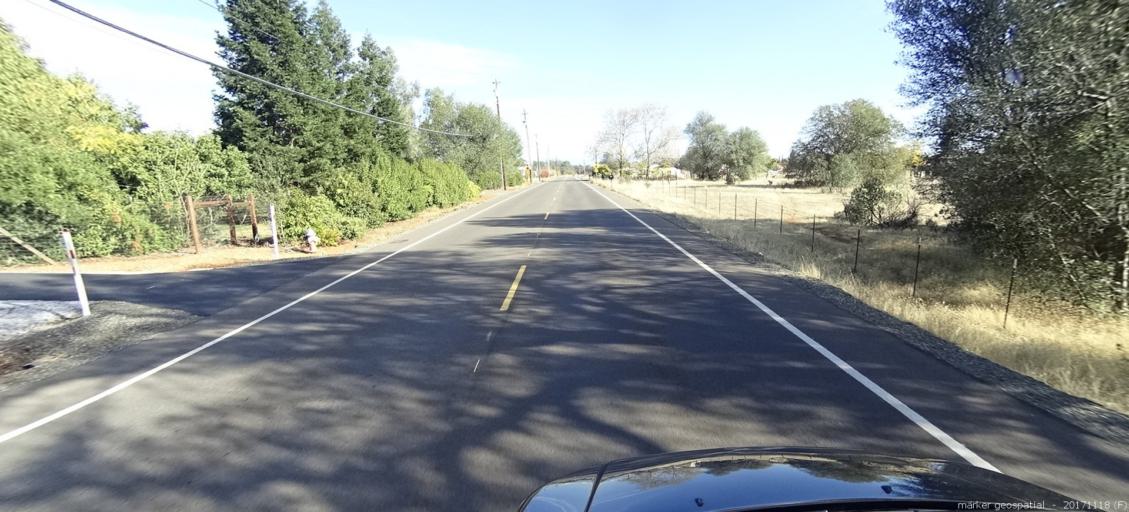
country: US
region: California
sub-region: Shasta County
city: Anderson
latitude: 40.4779
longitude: -122.4010
